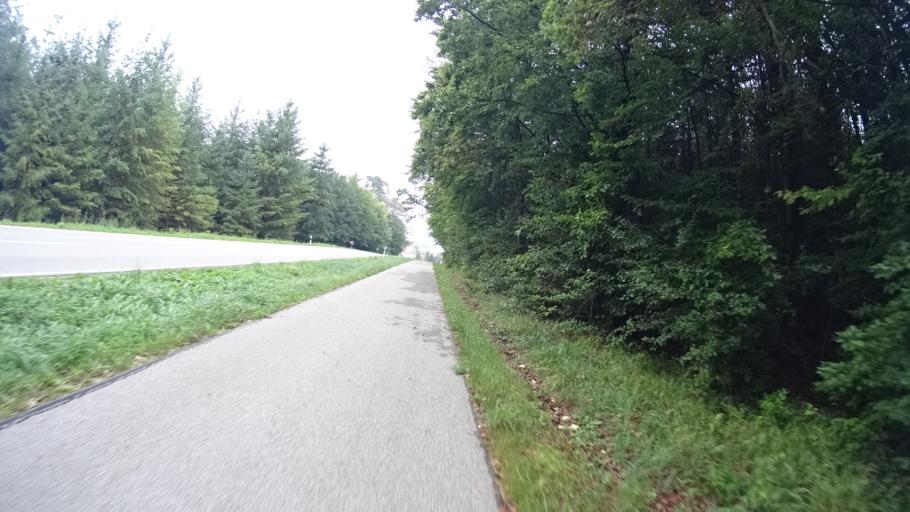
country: DE
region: Bavaria
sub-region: Upper Bavaria
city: Denkendorf
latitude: 48.9101
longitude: 11.4567
